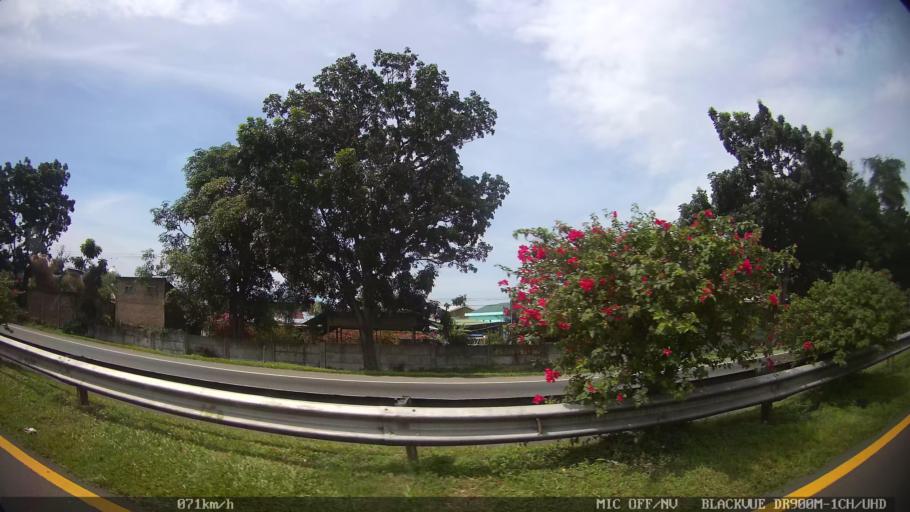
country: ID
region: North Sumatra
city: Medan
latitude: 3.6443
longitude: 98.6903
